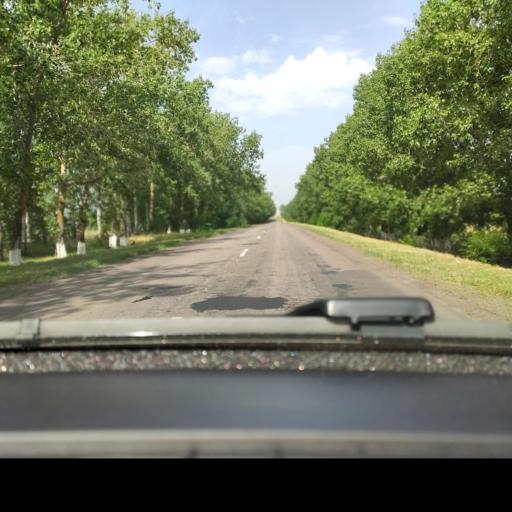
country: RU
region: Voronezj
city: Davydovka
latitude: 51.2461
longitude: 39.5544
